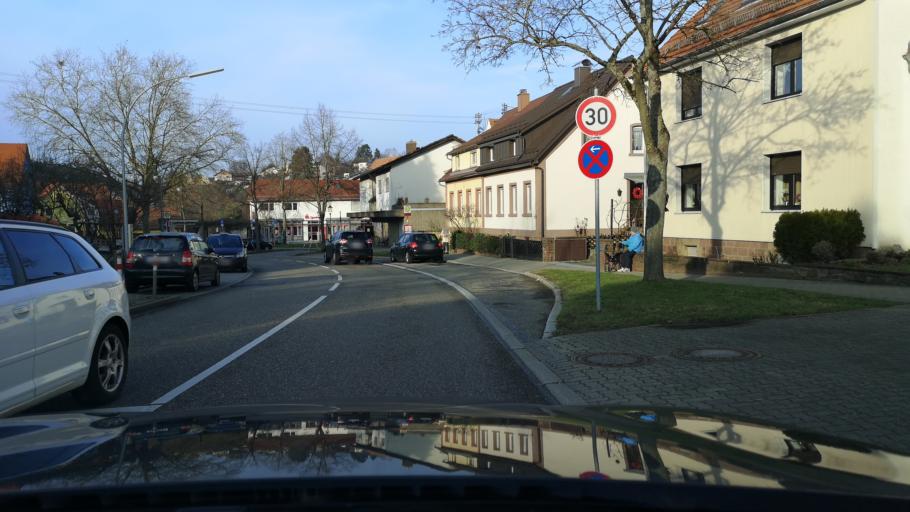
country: DE
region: Baden-Wuerttemberg
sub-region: Karlsruhe Region
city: Ettlingen
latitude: 48.9549
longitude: 8.4704
